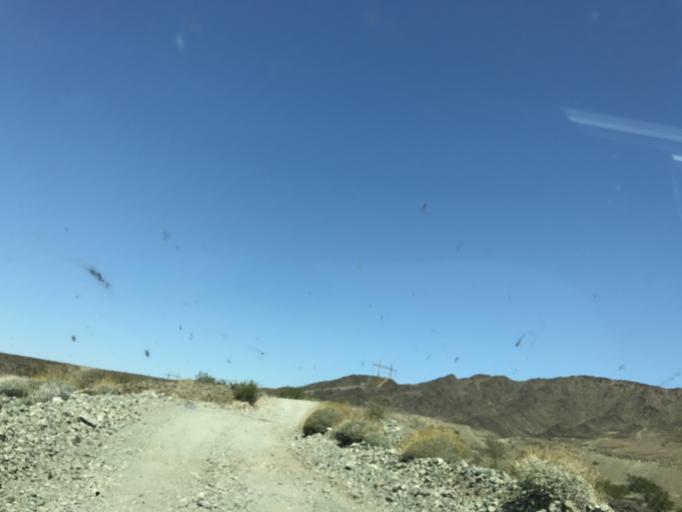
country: US
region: California
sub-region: Riverside County
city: Mesa Verde
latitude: 33.4956
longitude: -114.8353
